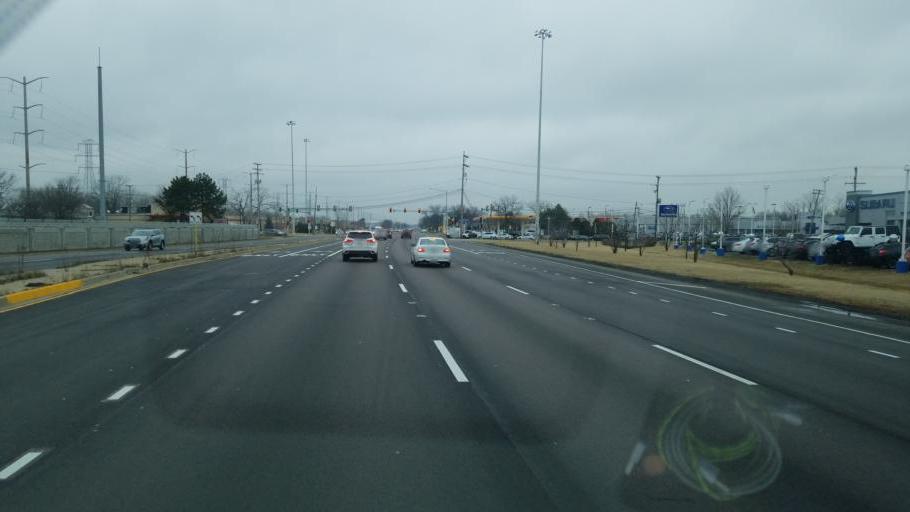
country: US
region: Illinois
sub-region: Lake County
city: Highwood
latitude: 42.1878
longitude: -87.8244
